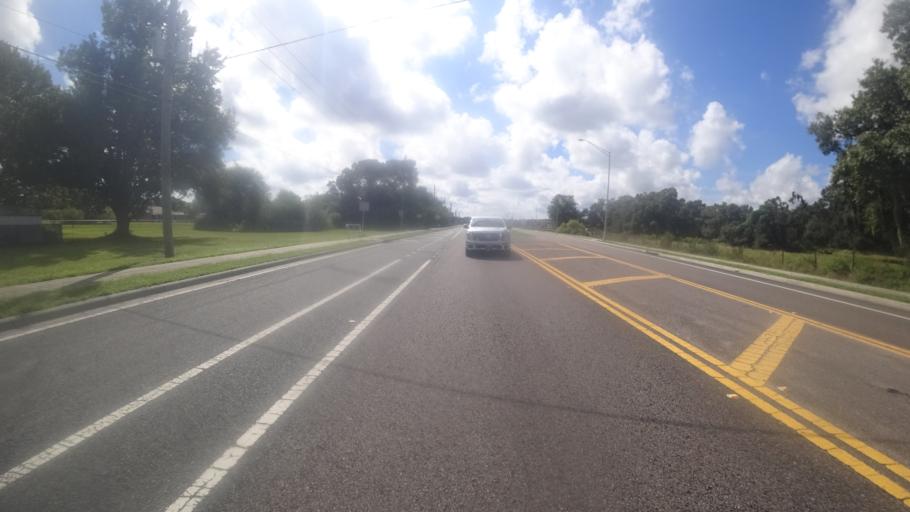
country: US
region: Florida
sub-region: Manatee County
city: Ellenton
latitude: 27.4887
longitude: -82.4336
